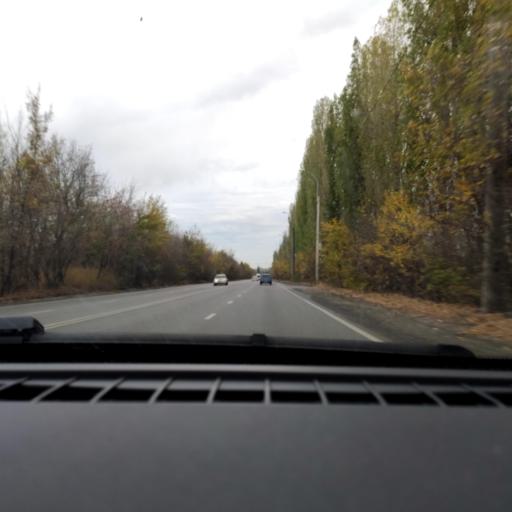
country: RU
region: Voronezj
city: Maslovka
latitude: 51.6067
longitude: 39.2554
